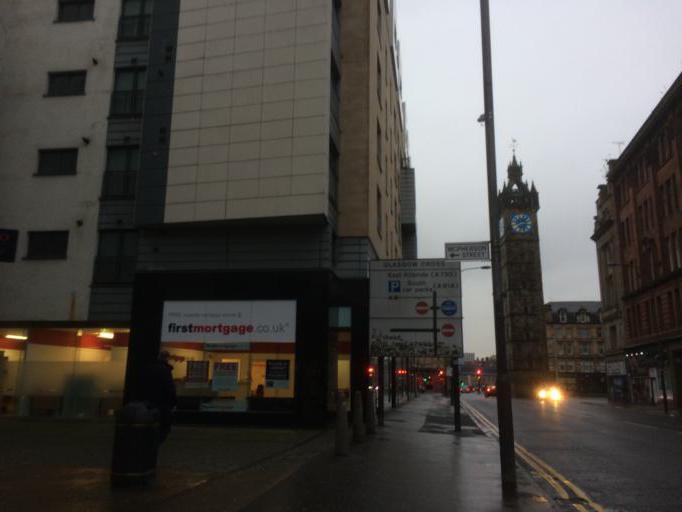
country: GB
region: Scotland
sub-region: Glasgow City
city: Glasgow
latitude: 55.8575
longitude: -4.2428
